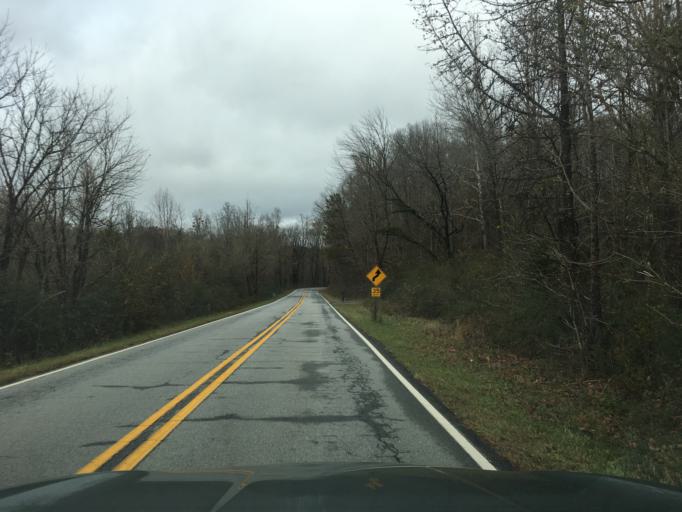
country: US
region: North Carolina
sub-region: Rutherford County
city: Rutherfordton
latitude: 35.3060
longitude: -81.9854
